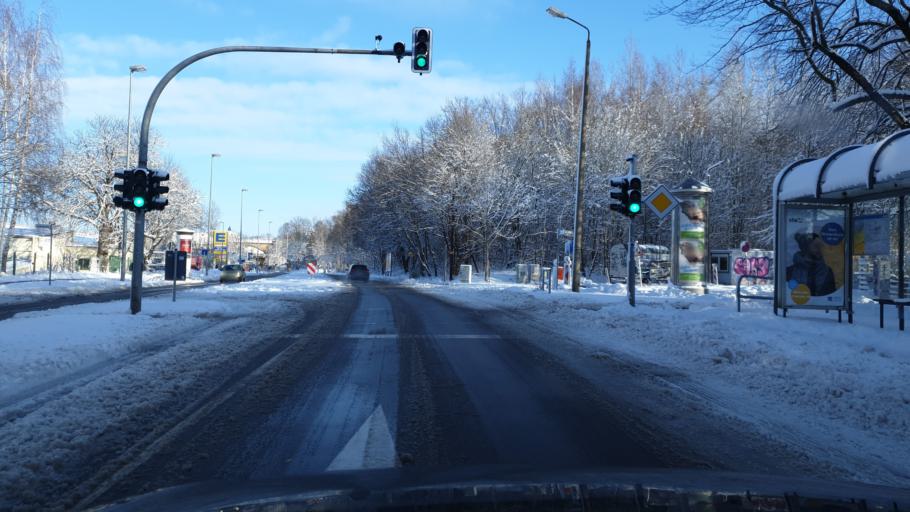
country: DE
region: Saxony
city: Chemnitz
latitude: 50.8503
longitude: 12.9289
